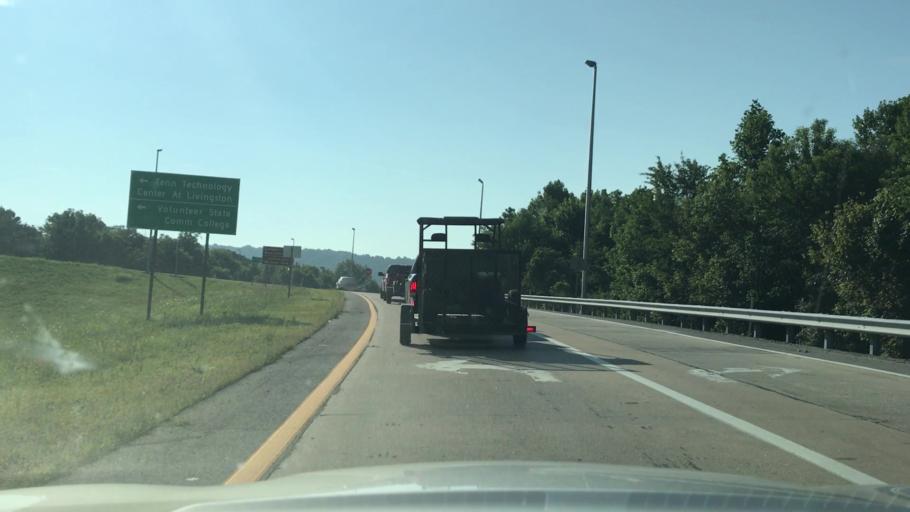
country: US
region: Tennessee
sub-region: Putnam County
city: Cookeville
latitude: 36.1336
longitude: -85.4812
